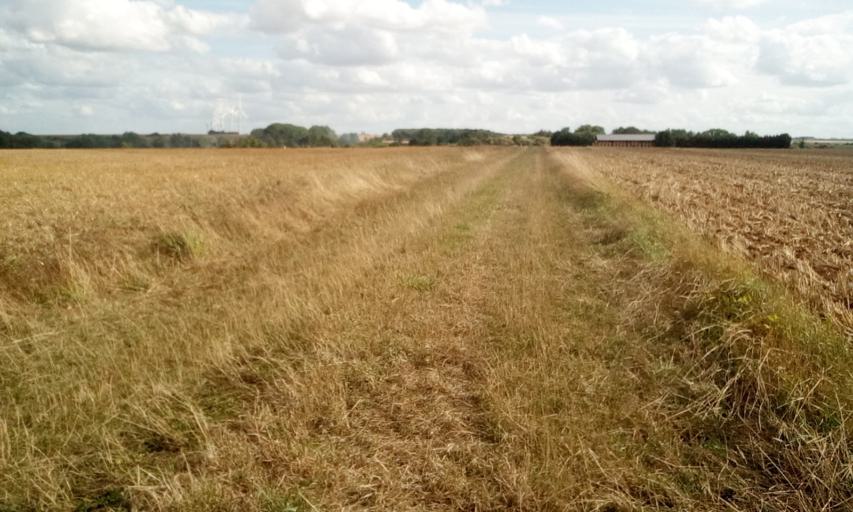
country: FR
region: Lower Normandy
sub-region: Departement du Calvados
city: Saint-Sylvain
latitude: 49.0765
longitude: -0.1971
